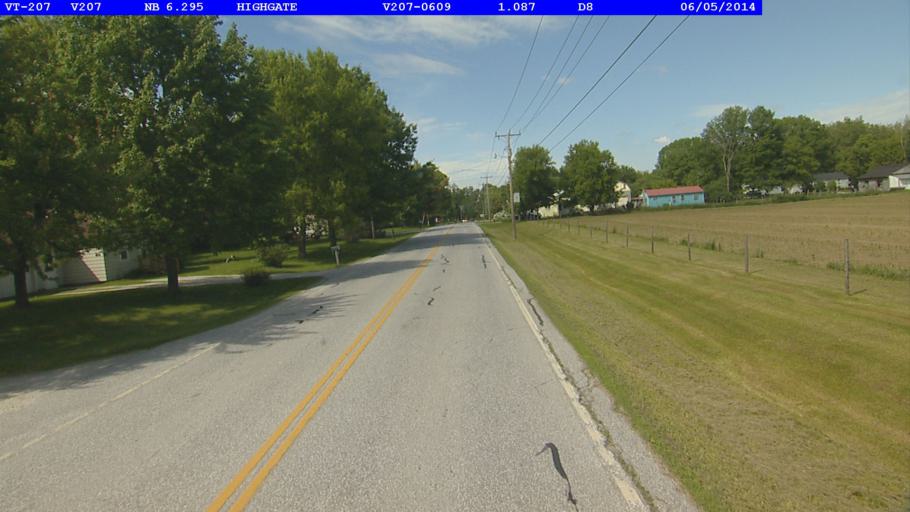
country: US
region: Vermont
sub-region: Franklin County
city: Swanton
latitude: 44.9263
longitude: -73.0508
